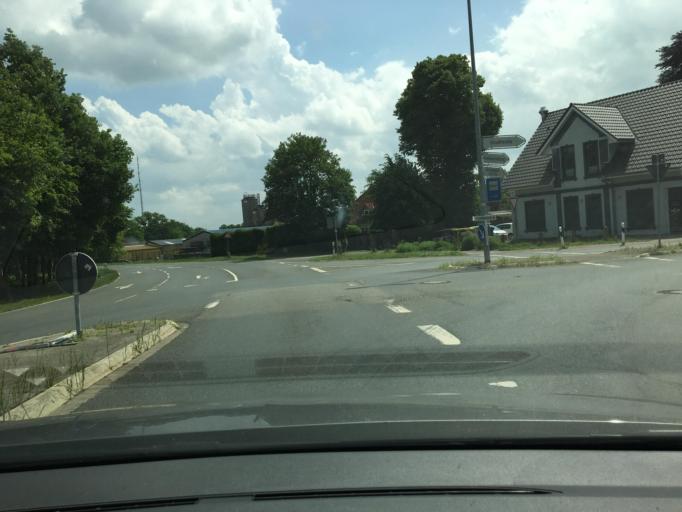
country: DE
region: Lower Saxony
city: Osterholz-Scharmbeck
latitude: 53.2493
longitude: 8.8161
